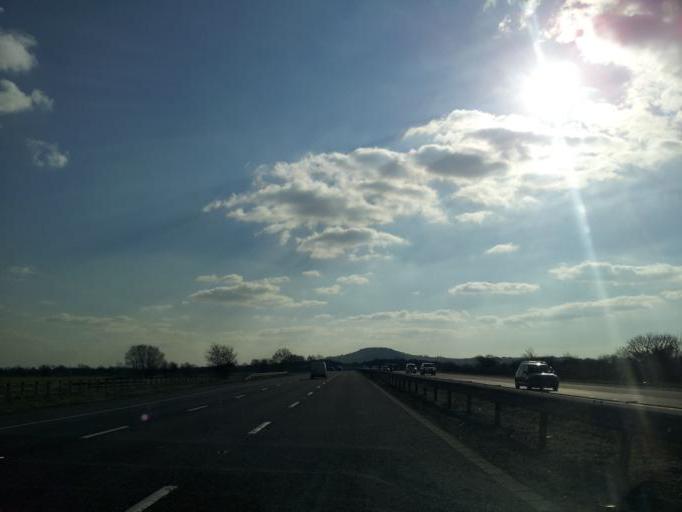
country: GB
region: England
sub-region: North Somerset
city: Hutton
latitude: 51.2823
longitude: -2.9067
